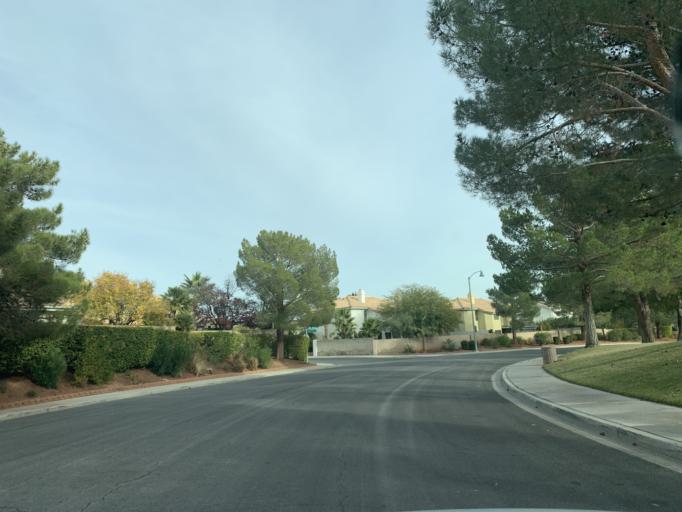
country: US
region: Nevada
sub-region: Clark County
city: Summerlin South
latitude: 36.1412
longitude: -115.3019
